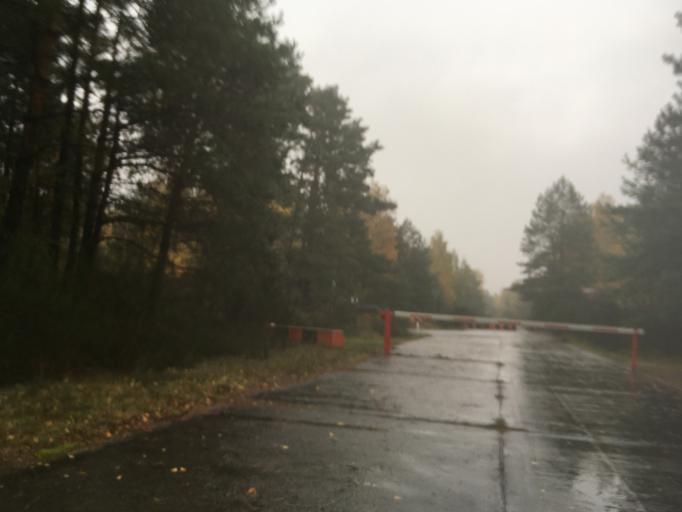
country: DE
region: Brandenburg
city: Halbe
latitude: 52.0321
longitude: 13.7677
